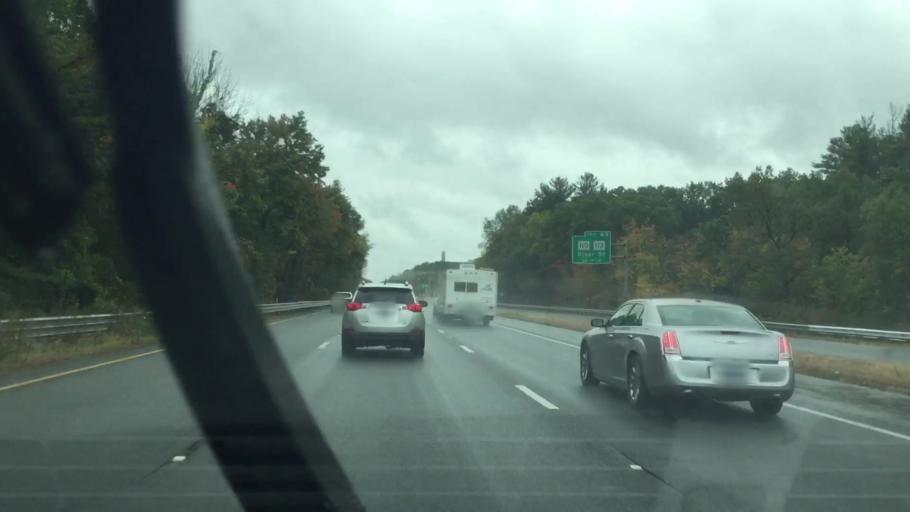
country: US
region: Massachusetts
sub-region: Essex County
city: Haverhill
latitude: 42.7831
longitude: -71.1160
